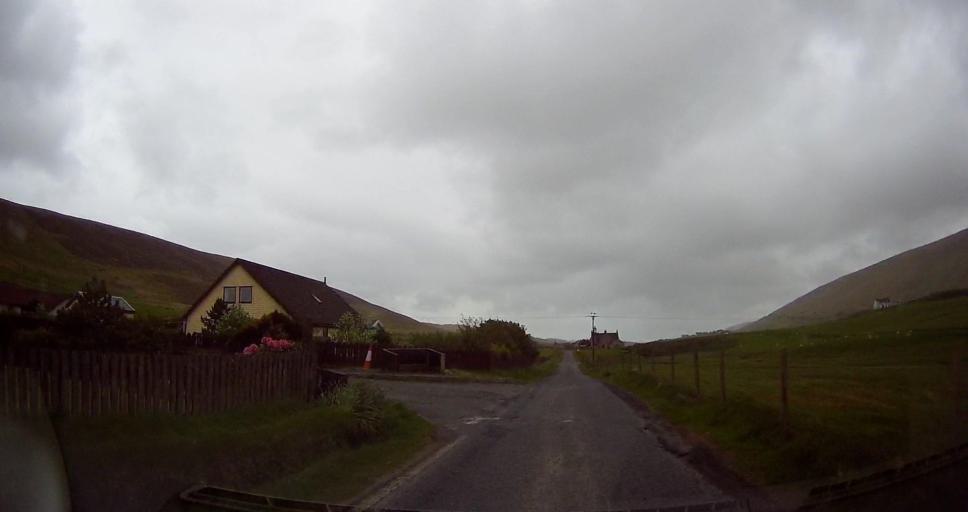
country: GB
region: Scotland
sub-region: Shetland Islands
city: Lerwick
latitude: 60.2588
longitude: -1.2881
